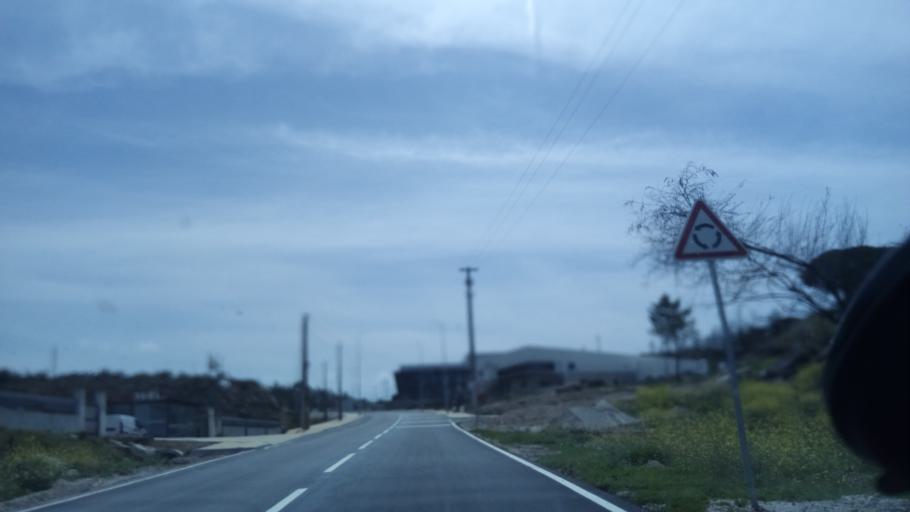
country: PT
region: Viseu
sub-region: Mangualde
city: Mangualde
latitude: 40.6102
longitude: -7.7889
